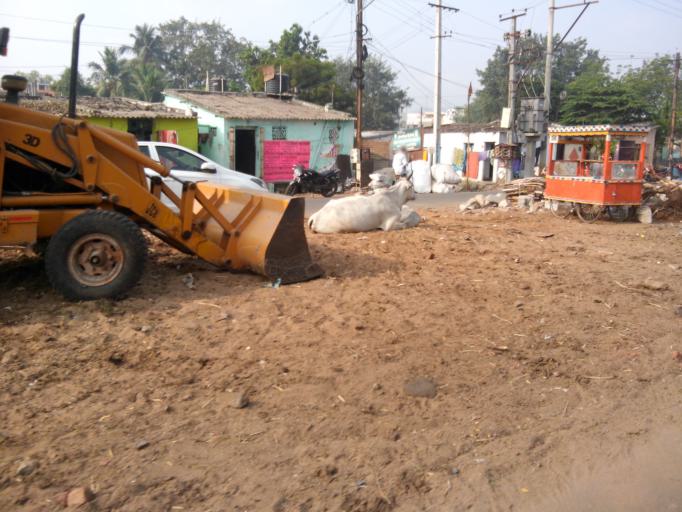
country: IN
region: Andhra Pradesh
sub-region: Krishna
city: Vijayawada
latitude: 16.5088
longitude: 80.6222
